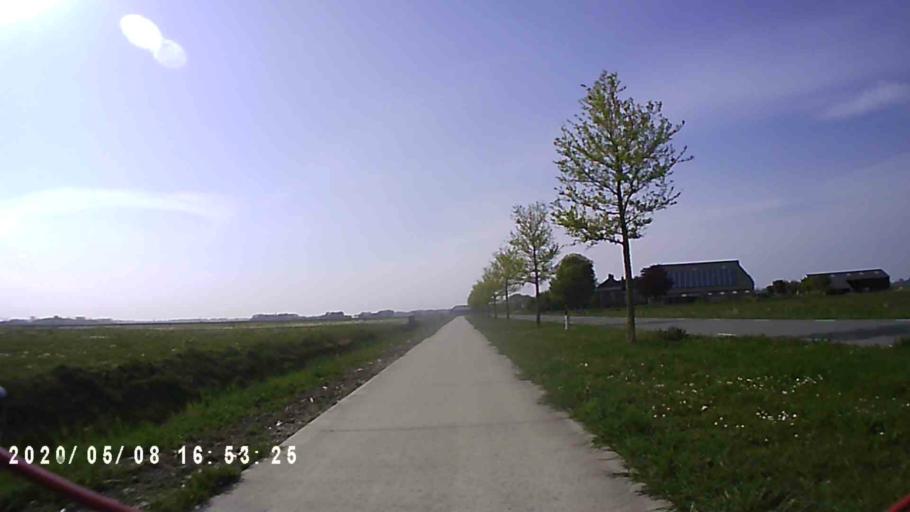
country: NL
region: Groningen
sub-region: Gemeente Bedum
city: Bedum
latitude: 53.3868
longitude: 6.6252
